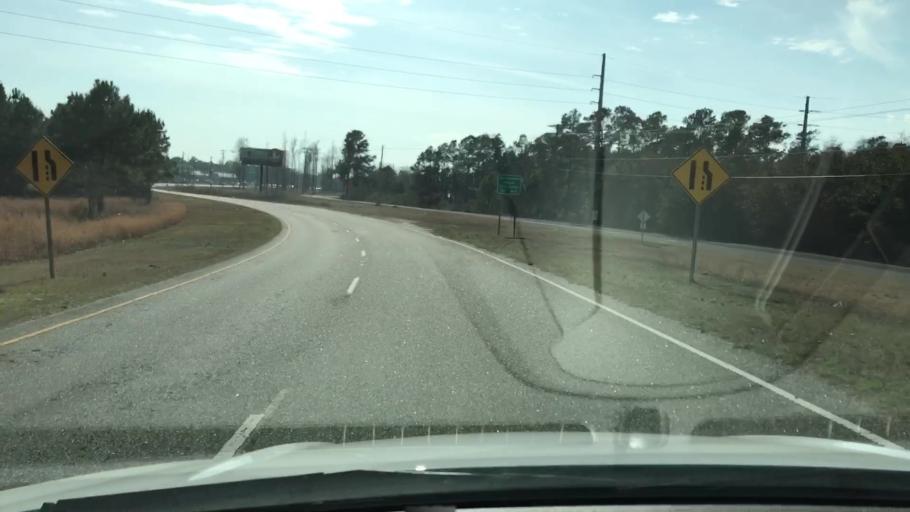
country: US
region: South Carolina
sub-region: Georgetown County
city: Murrells Inlet
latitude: 33.5727
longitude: -79.0316
